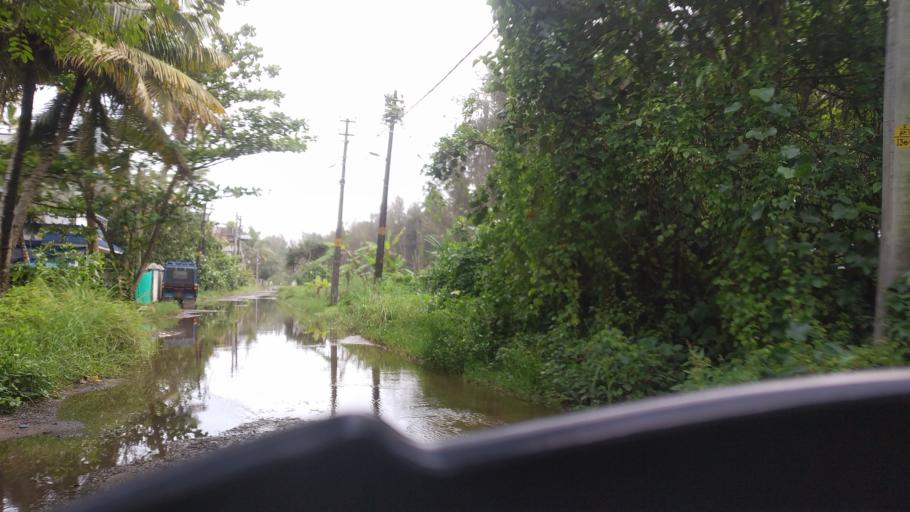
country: IN
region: Kerala
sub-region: Ernakulam
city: Elur
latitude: 10.1056
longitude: 76.1886
